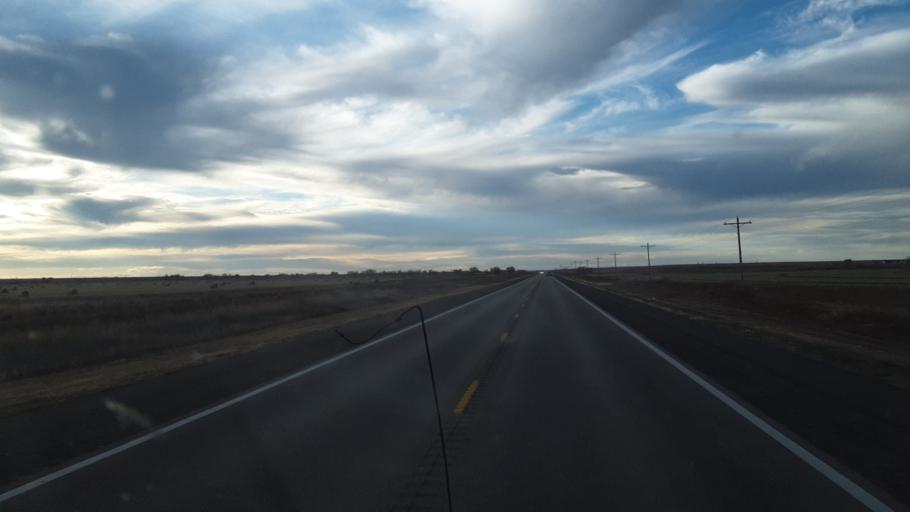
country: US
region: Kansas
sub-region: Hamilton County
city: Syracuse
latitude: 38.0187
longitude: -101.8986
